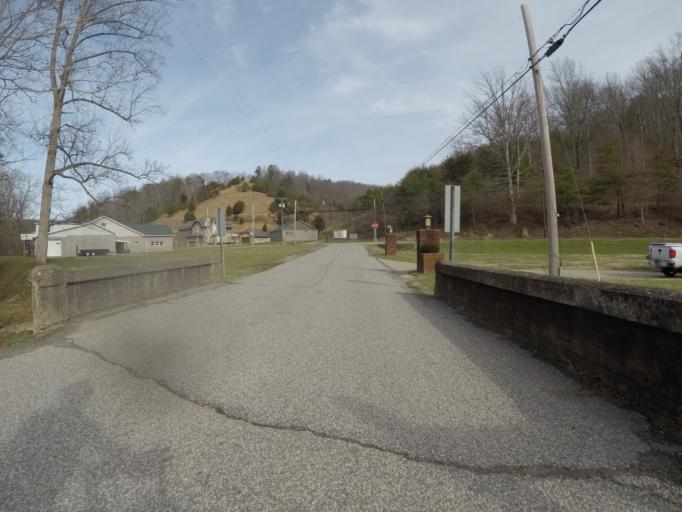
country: US
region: West Virginia
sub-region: Cabell County
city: Pea Ridge
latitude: 38.3587
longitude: -82.3714
